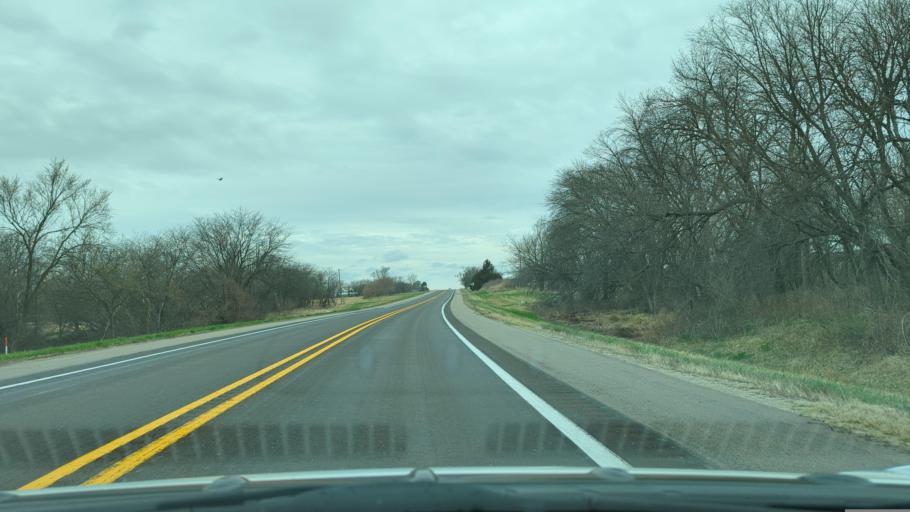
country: US
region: Nebraska
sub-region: Lancaster County
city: Waverly
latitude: 40.9503
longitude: -96.4543
